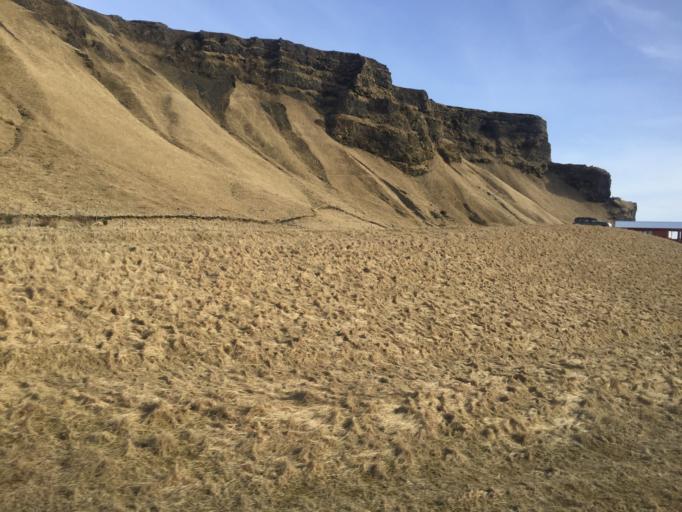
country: IS
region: South
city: Vestmannaeyjar
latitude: 63.4070
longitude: -19.0480
